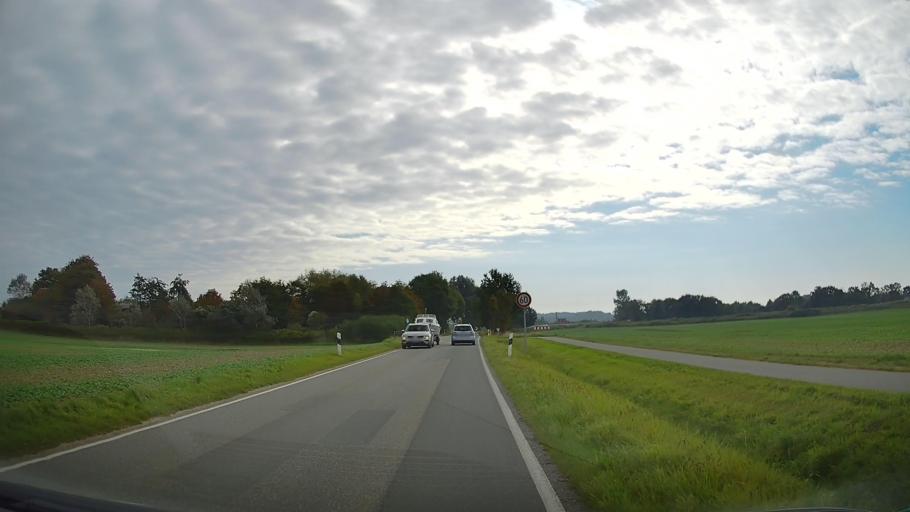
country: DE
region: Schleswig-Holstein
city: Blekendorf
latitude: 54.3390
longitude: 10.6432
